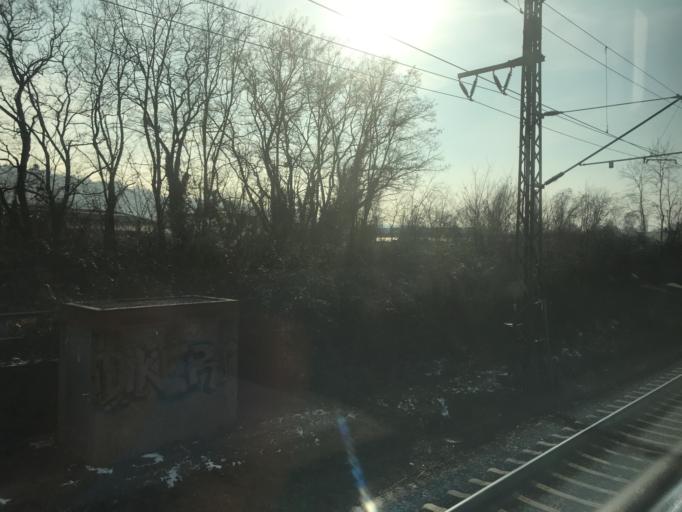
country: DE
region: Rheinland-Pfalz
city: Konz
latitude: 49.7048
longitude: 6.5833
